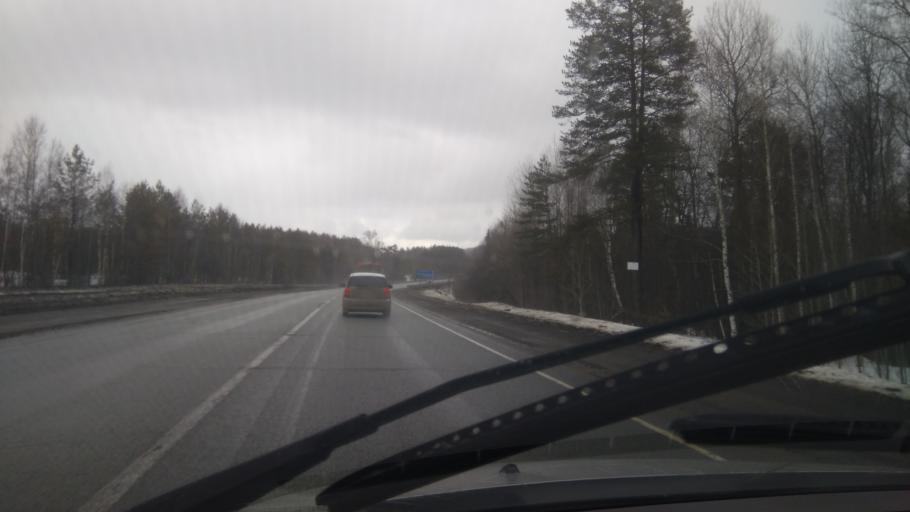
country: RU
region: Sverdlovsk
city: Ufimskiy
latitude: 56.7802
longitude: 58.2606
